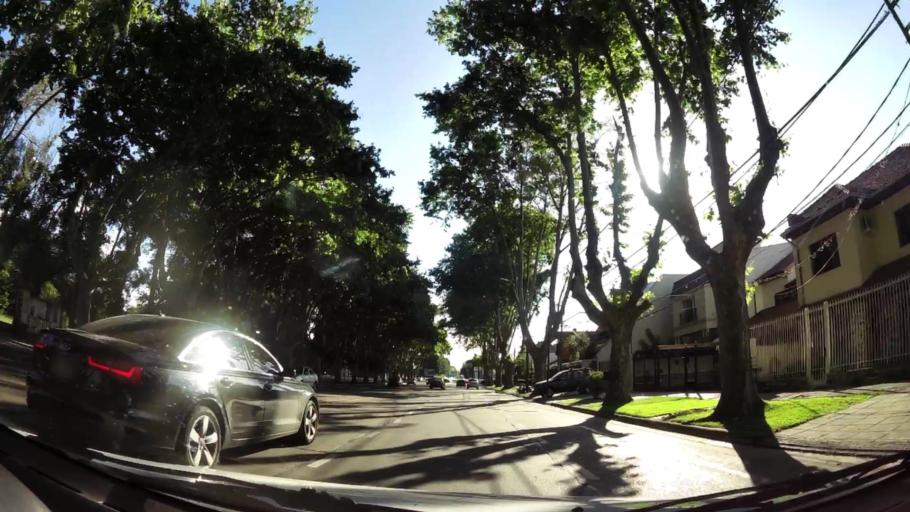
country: AR
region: Buenos Aires
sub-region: Partido de San Isidro
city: San Isidro
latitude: -34.4813
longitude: -58.5261
